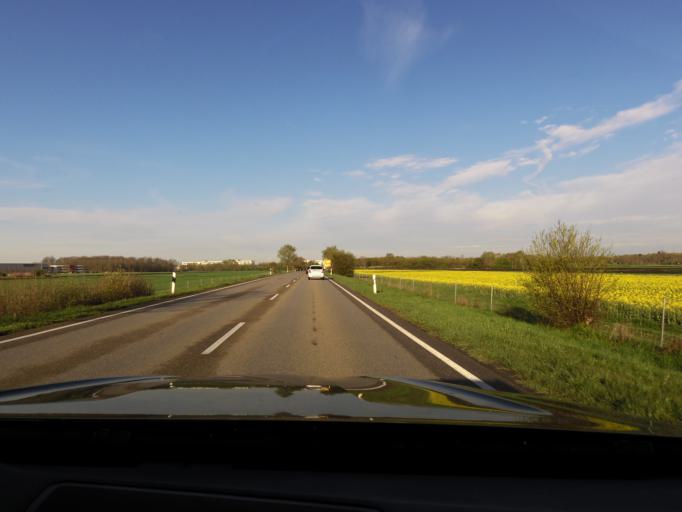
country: DE
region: Bavaria
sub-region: Upper Bavaria
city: Oberding
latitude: 48.3596
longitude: 11.8428
